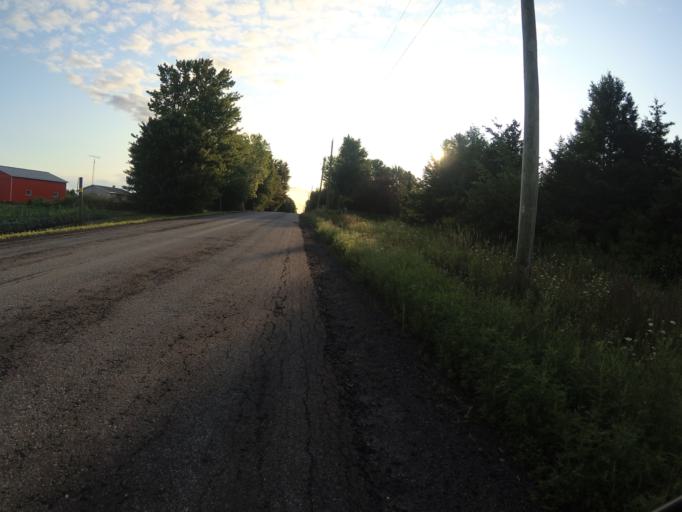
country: CA
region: Ontario
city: Ottawa
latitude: 45.1499
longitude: -75.4293
